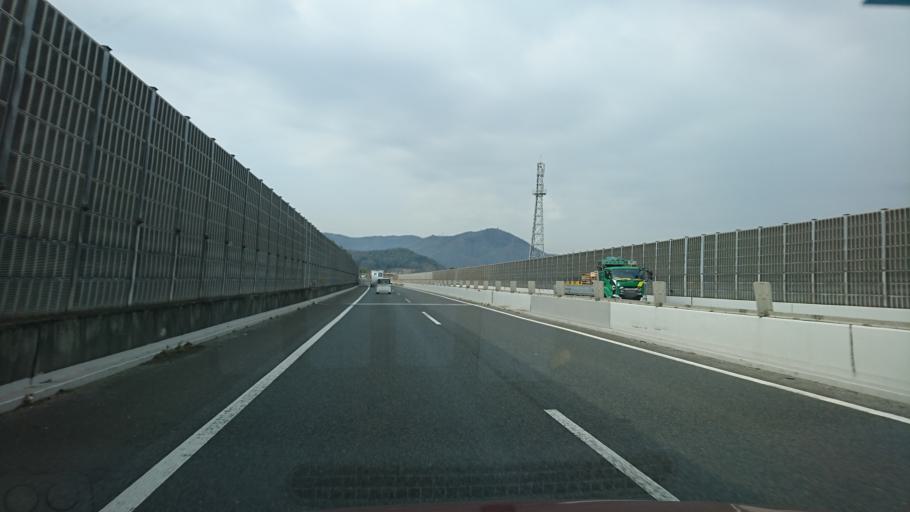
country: JP
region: Hiroshima
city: Fukuyama
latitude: 34.5170
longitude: 133.3774
